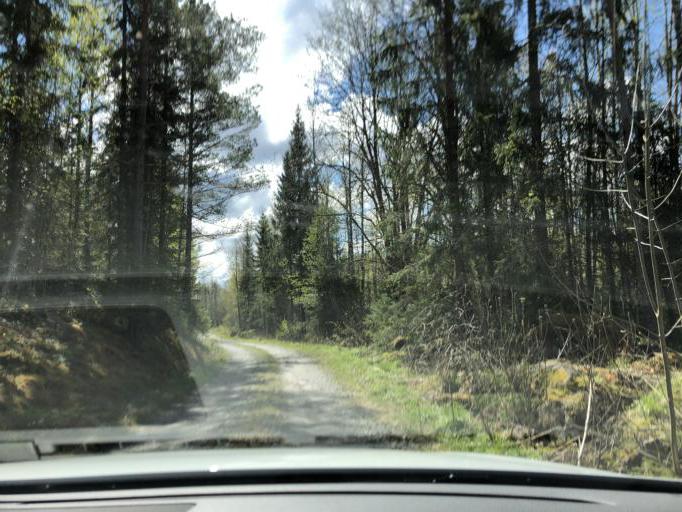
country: SE
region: Uppsala
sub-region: Heby Kommun
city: Tarnsjo
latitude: 60.2405
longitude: 16.7048
